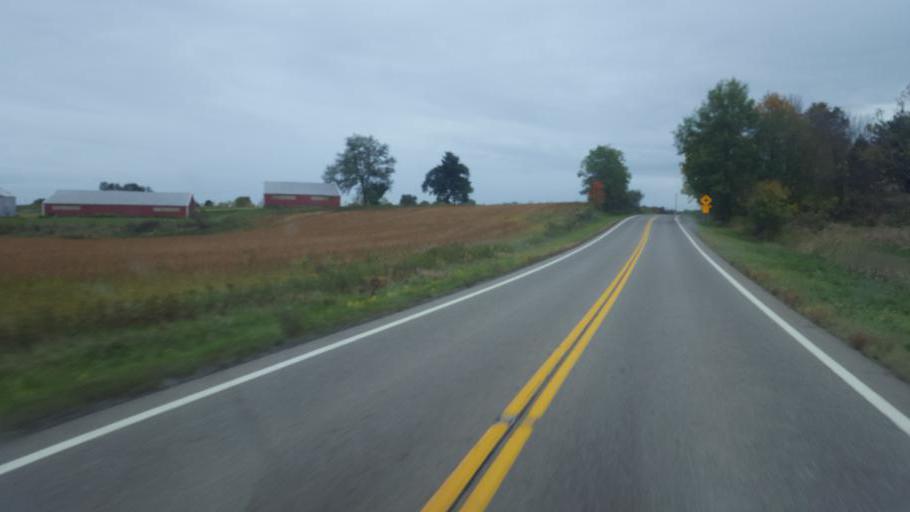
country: US
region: Ohio
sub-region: Ashland County
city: Ashland
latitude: 40.9551
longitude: -82.3712
